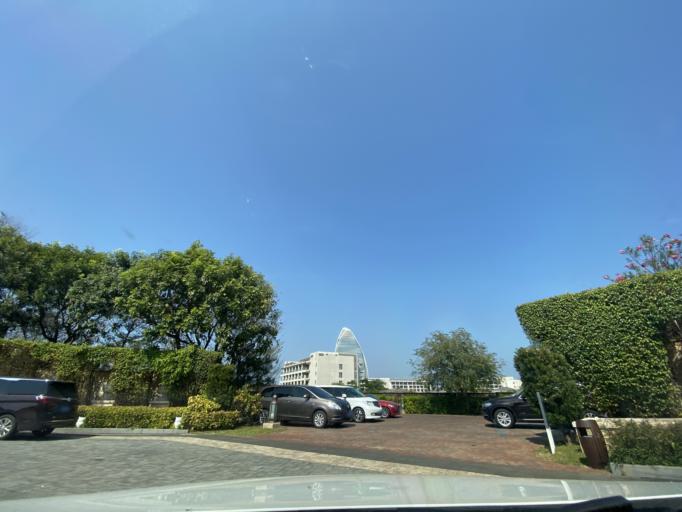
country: CN
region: Hainan
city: Haitangwan
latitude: 18.3503
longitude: 109.7374
